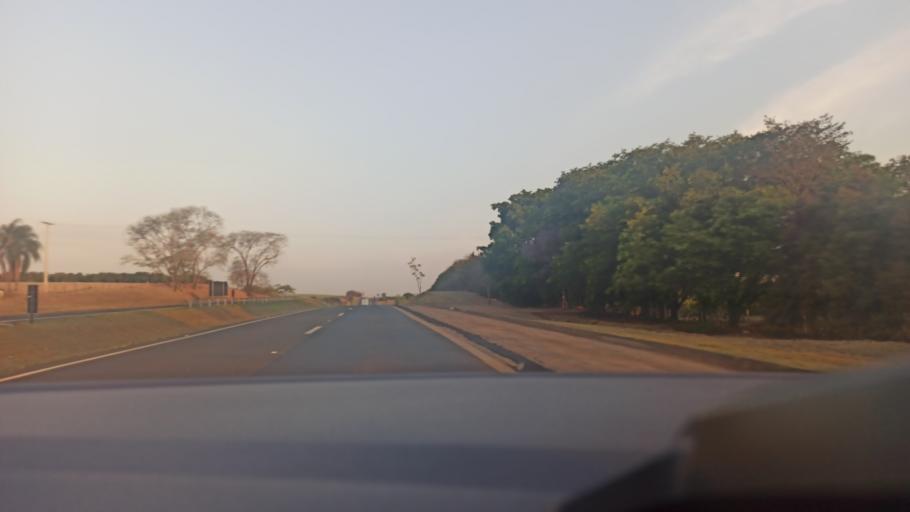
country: BR
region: Sao Paulo
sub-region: Santa Adelia
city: Santa Adelia
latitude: -21.3943
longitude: -48.7161
